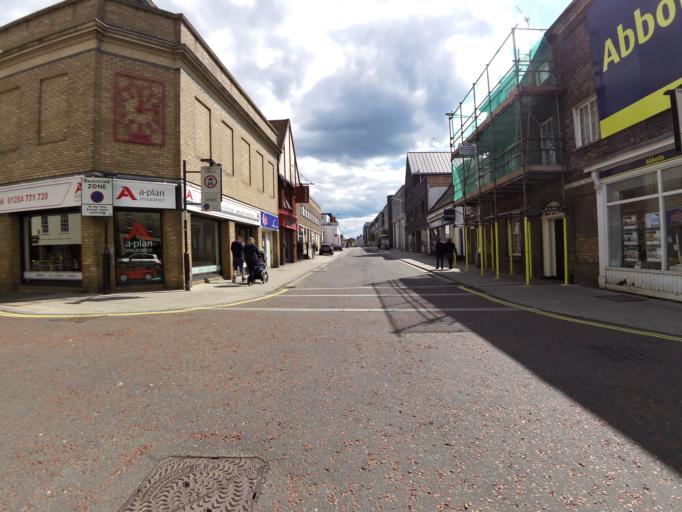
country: GB
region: England
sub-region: Suffolk
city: Bury St Edmunds
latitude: 52.2469
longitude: 0.7112
